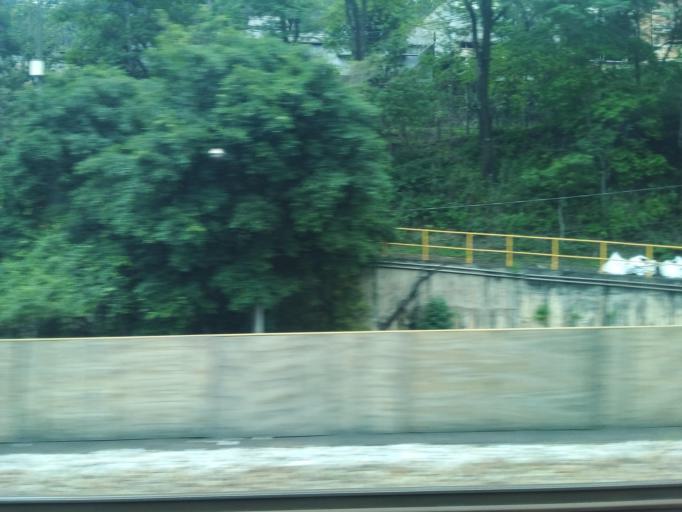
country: BR
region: Minas Gerais
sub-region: Joao Monlevade
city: Joao Monlevade
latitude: -19.8357
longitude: -43.1300
